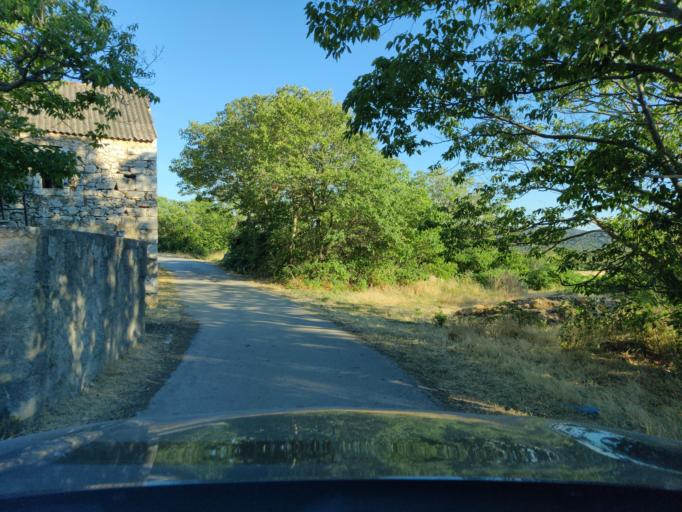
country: HR
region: Sibensko-Kniniska
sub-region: Grad Sibenik
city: Pirovac
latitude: 43.8633
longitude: 15.7170
